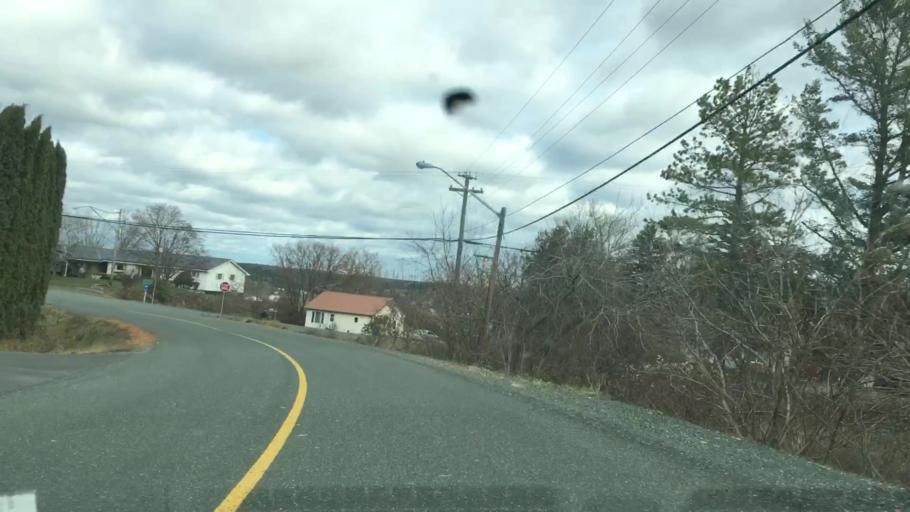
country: CA
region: New Brunswick
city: Florenceville-Bristol
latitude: 46.2906
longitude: -67.5334
